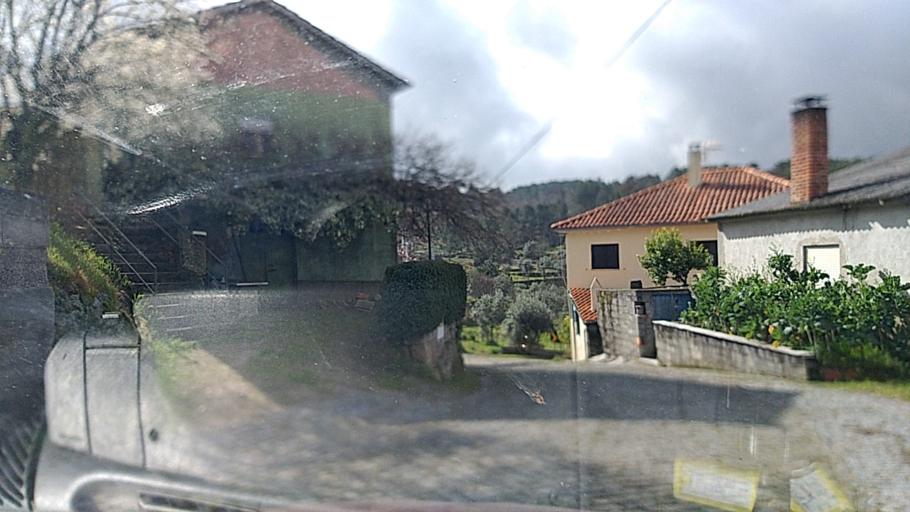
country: PT
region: Guarda
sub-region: Fornos de Algodres
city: Fornos de Algodres
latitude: 40.6621
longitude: -7.6468
